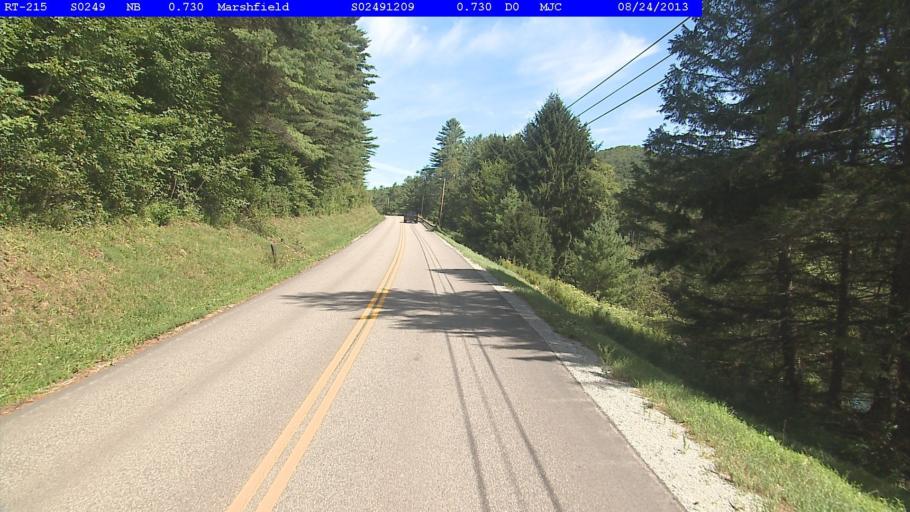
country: US
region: Vermont
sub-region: Caledonia County
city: Hardwick
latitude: 44.3586
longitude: -72.3387
